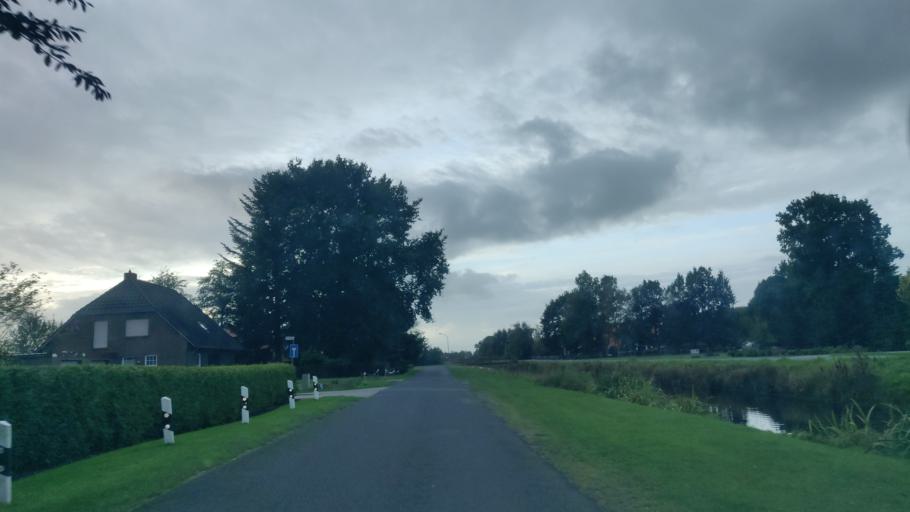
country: DE
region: Lower Saxony
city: Rechtsupweg
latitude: 53.4856
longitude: 7.3972
